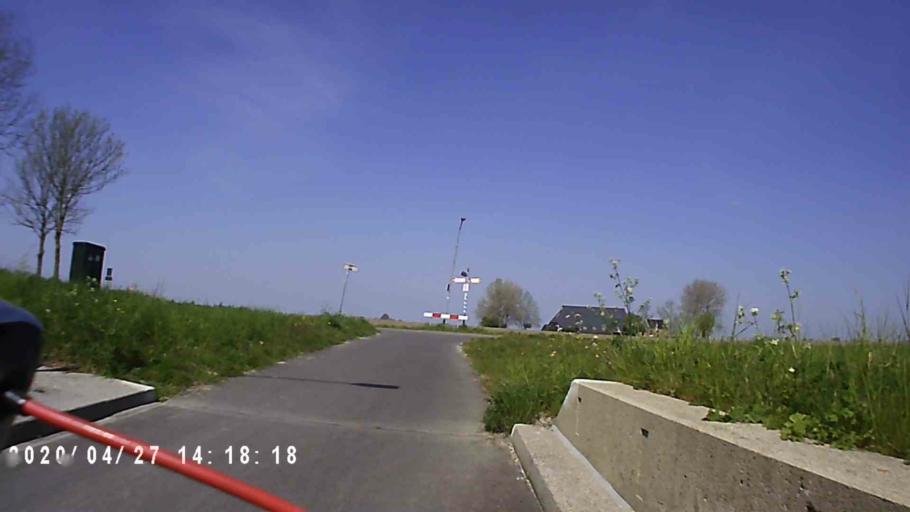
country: NL
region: Groningen
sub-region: Gemeente De Marne
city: Ulrum
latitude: 53.3637
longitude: 6.3867
